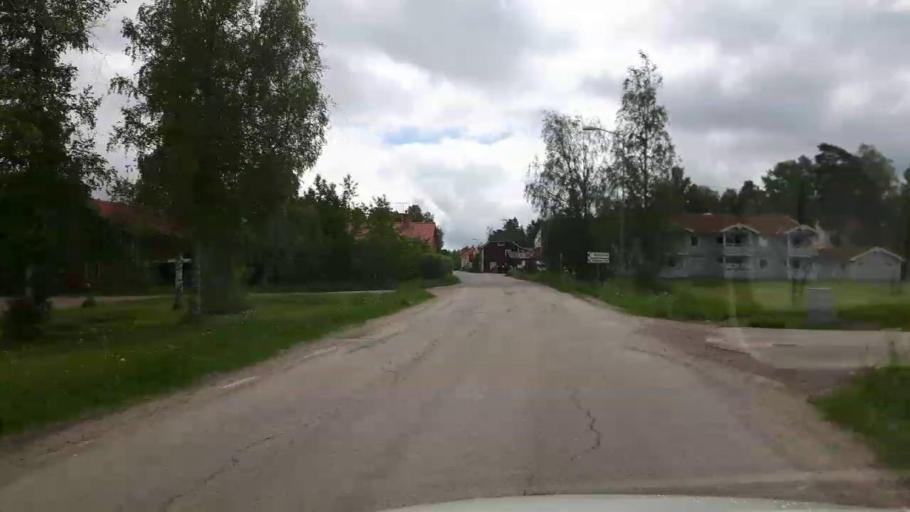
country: SE
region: Gaevleborg
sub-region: Ovanakers Kommun
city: Alfta
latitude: 61.3387
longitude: 15.9495
